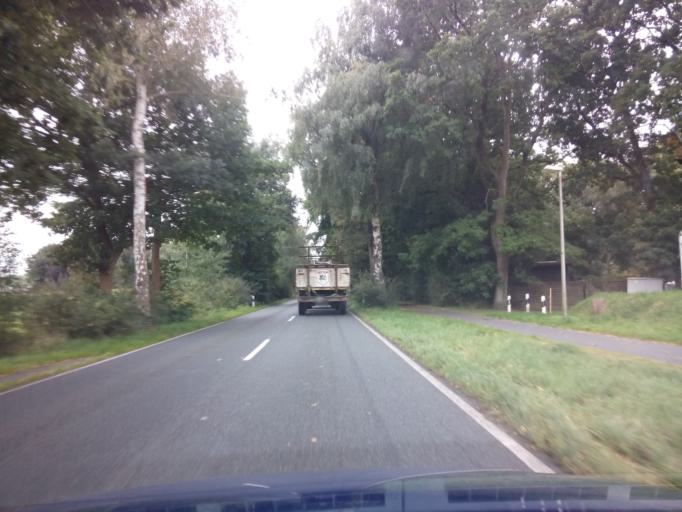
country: DE
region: Lower Saxony
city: Lubberstedt
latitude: 53.3366
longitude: 8.8180
